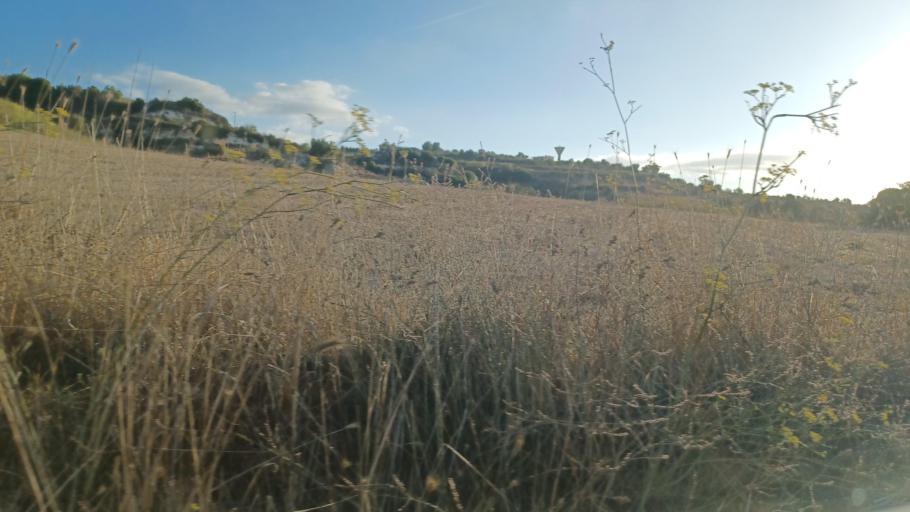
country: CY
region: Pafos
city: Mesogi
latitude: 34.8740
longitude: 32.4975
